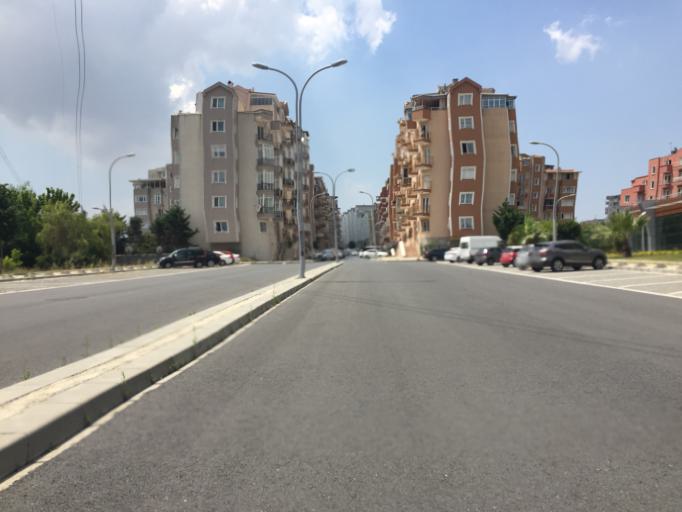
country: TR
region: Istanbul
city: Esenyurt
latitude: 41.0775
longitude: 28.6694
